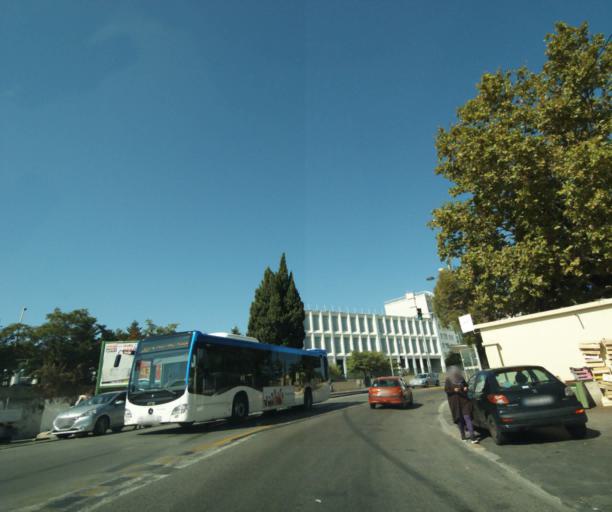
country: FR
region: Provence-Alpes-Cote d'Azur
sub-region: Departement des Bouches-du-Rhone
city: Marseille 13
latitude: 43.3309
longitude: 5.4045
